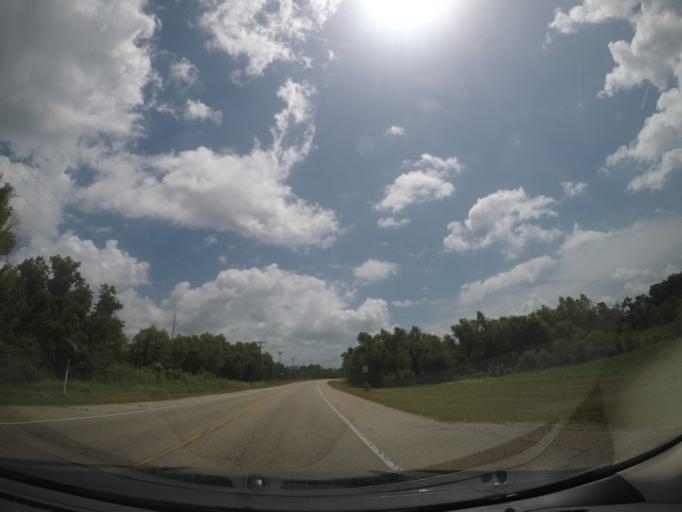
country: US
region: Mississippi
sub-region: Hancock County
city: Pearlington
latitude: 30.2285
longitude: -89.6772
